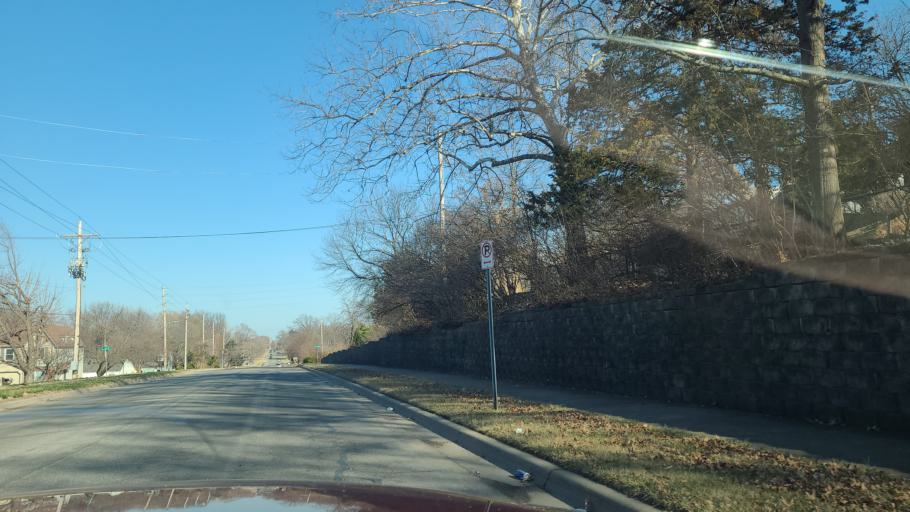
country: US
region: Kansas
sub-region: Douglas County
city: Lawrence
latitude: 38.9769
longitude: -95.2584
